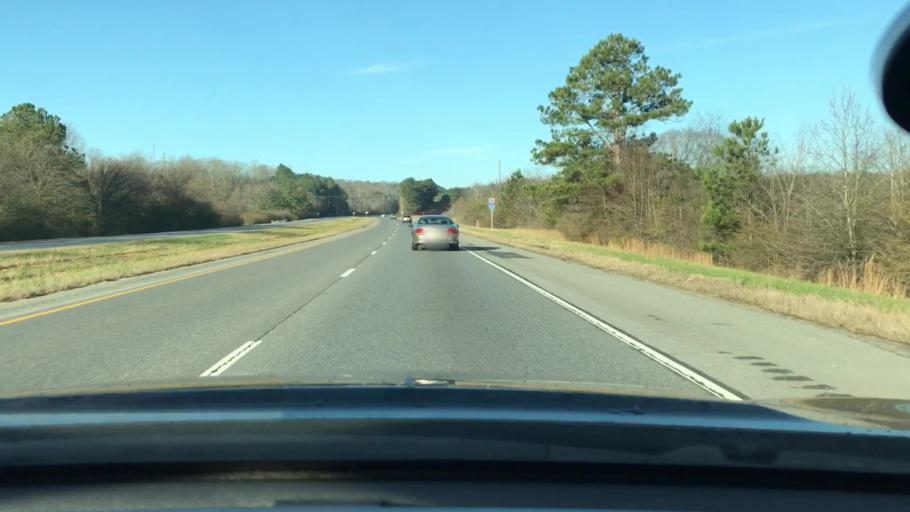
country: US
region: Alabama
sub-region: Shelby County
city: Harpersville
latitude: 33.3509
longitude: -86.4679
